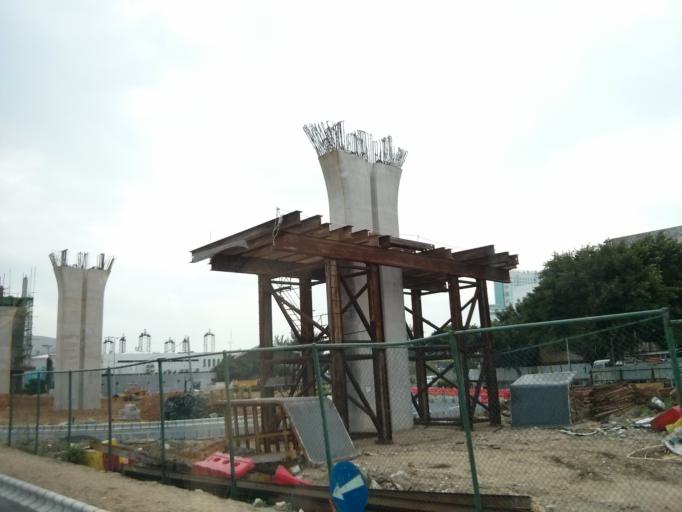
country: MO
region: Macau
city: Macau
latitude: 22.1636
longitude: 113.5725
